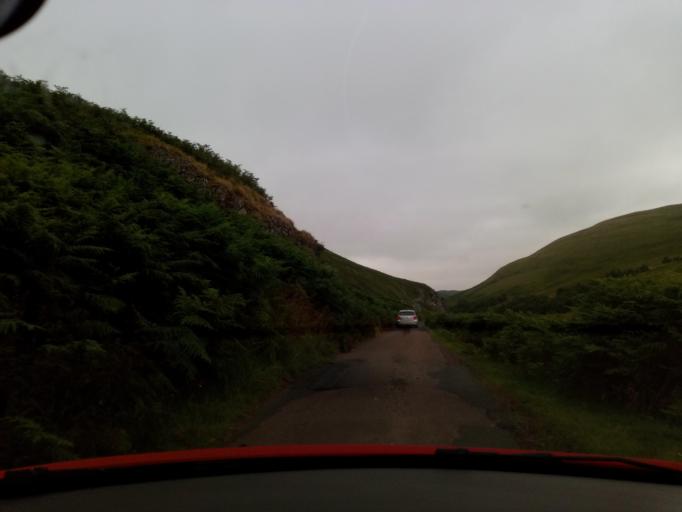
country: GB
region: England
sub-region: Northumberland
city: Rochester
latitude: 55.3662
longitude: -2.1970
